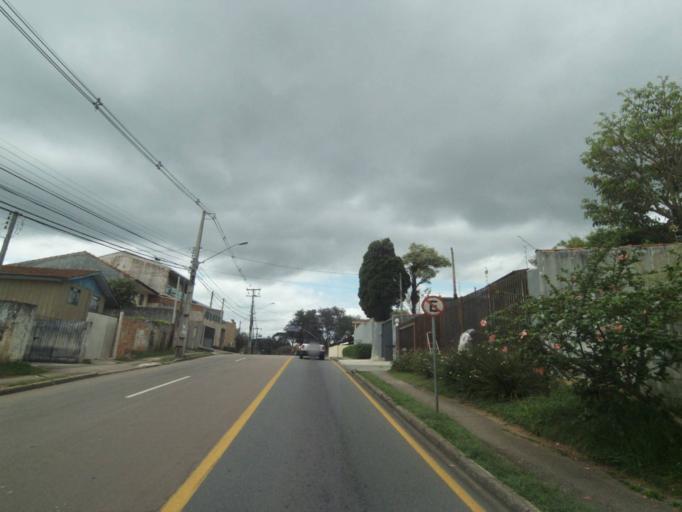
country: BR
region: Parana
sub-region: Curitiba
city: Curitiba
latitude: -25.3870
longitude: -49.2826
